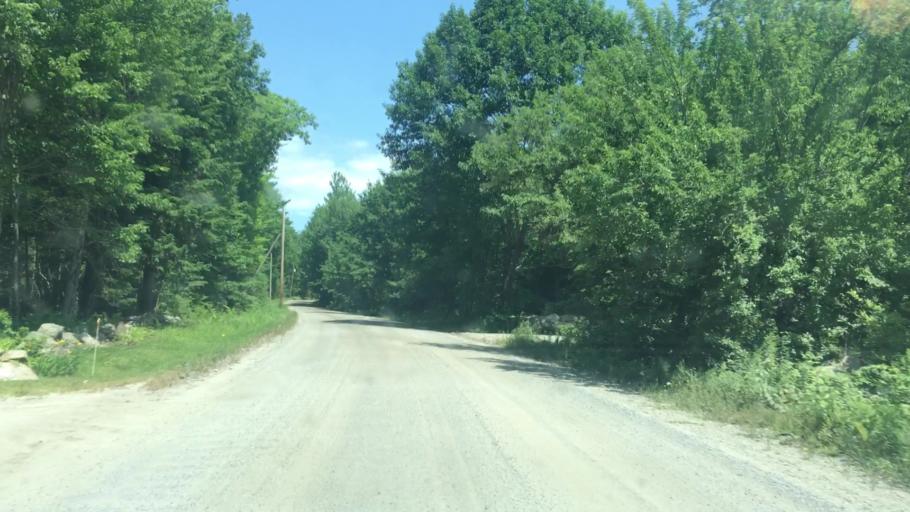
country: US
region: Maine
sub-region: Kennebec County
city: Monmouth
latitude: 44.2879
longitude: -70.0551
